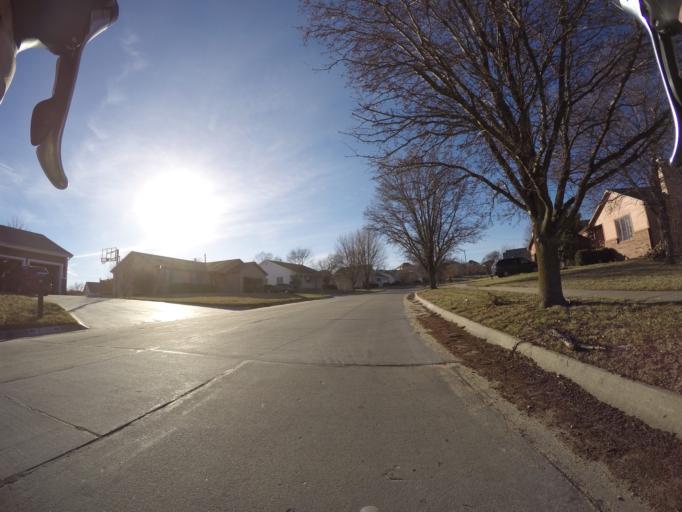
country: US
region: Kansas
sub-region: Riley County
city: Manhattan
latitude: 39.2132
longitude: -96.6216
